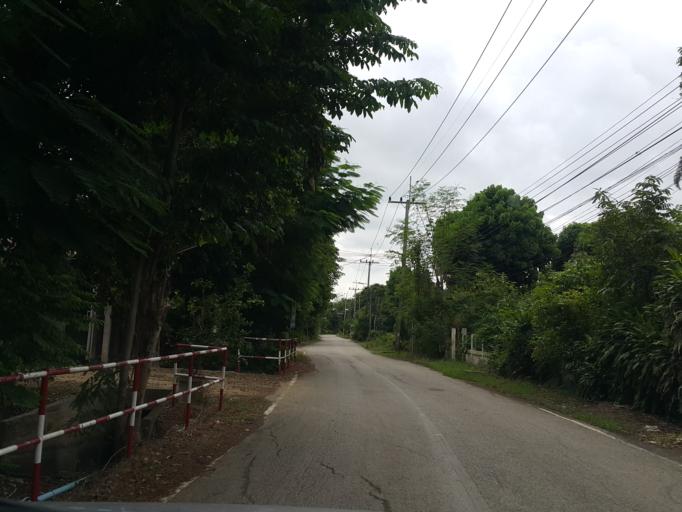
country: TH
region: Chiang Mai
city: San Kamphaeng
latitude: 18.7959
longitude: 99.1404
